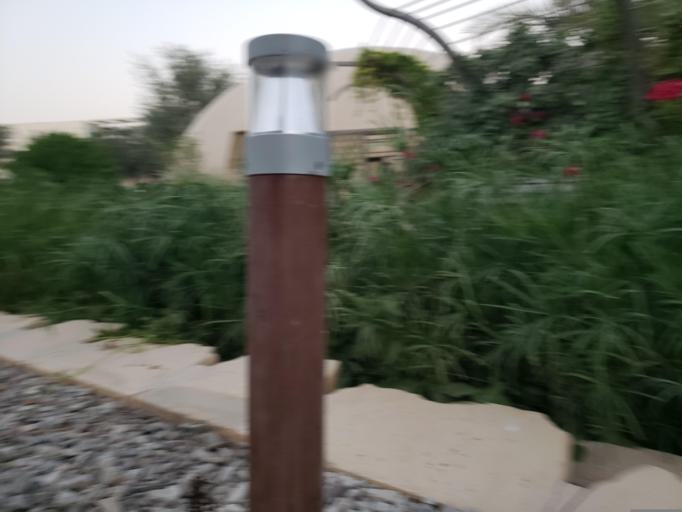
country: AE
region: Dubai
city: Dubai
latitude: 25.0305
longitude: 55.2795
